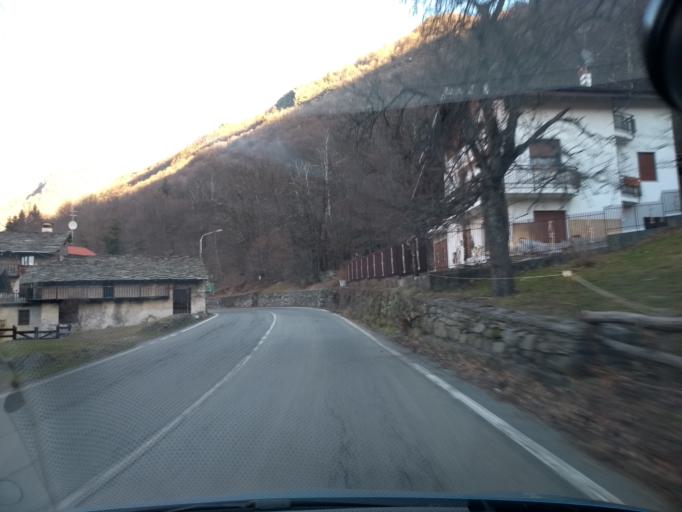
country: IT
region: Piedmont
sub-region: Provincia di Torino
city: Ceres
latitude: 45.3260
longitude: 7.3971
